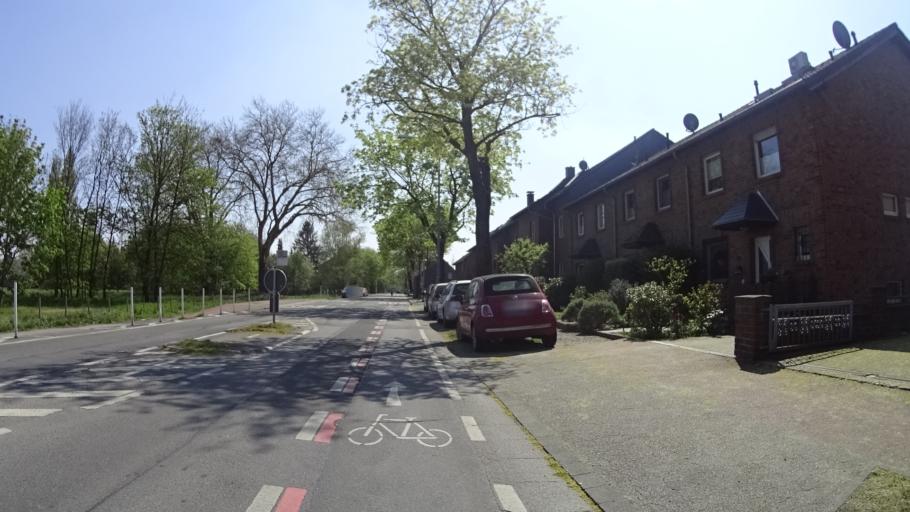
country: DE
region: North Rhine-Westphalia
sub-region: Regierungsbezirk Dusseldorf
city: Meerbusch
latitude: 51.3271
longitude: 6.6718
